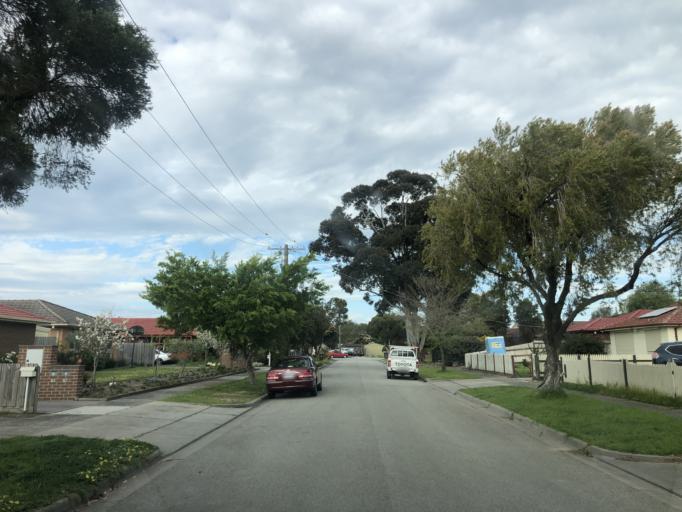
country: AU
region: Victoria
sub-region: Casey
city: Hampton Park
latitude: -38.0279
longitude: 145.2477
